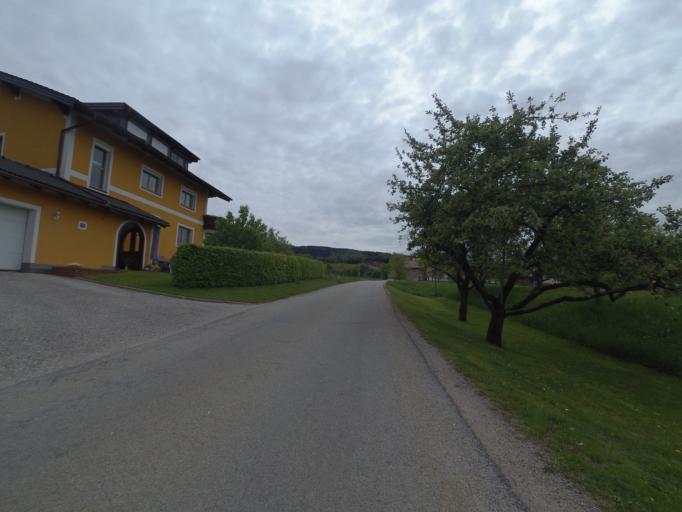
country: AT
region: Salzburg
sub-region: Politischer Bezirk Salzburg-Umgebung
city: Schleedorf
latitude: 47.9894
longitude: 13.1526
